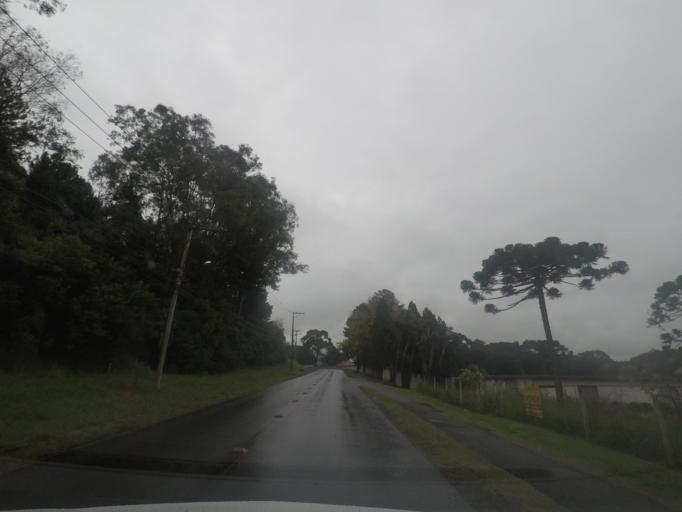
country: BR
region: Parana
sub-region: Quatro Barras
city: Quatro Barras
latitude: -25.3825
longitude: -49.1328
